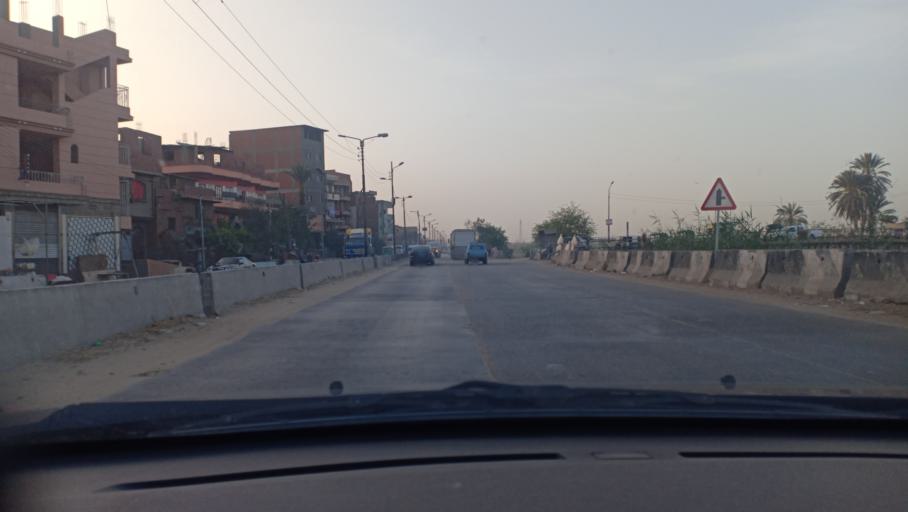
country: EG
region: Muhafazat al Gharbiyah
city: Zifta
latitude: 30.6820
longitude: 31.2817
